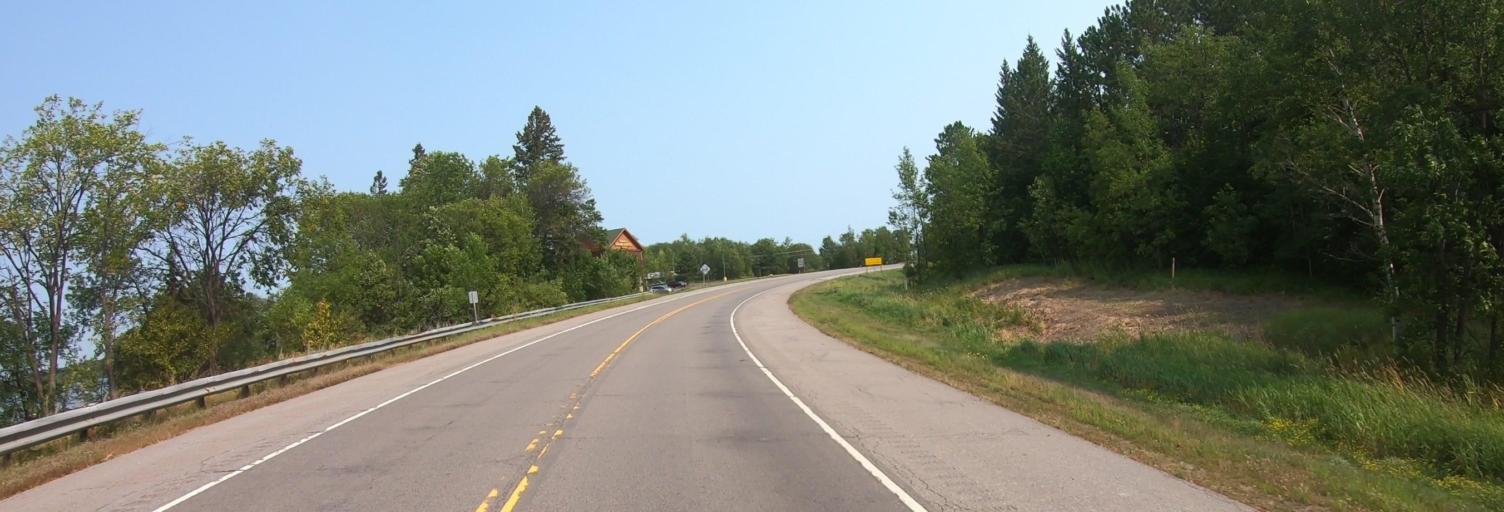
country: US
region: Minnesota
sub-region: Saint Louis County
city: Mountain Iron
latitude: 48.0617
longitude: -92.8310
